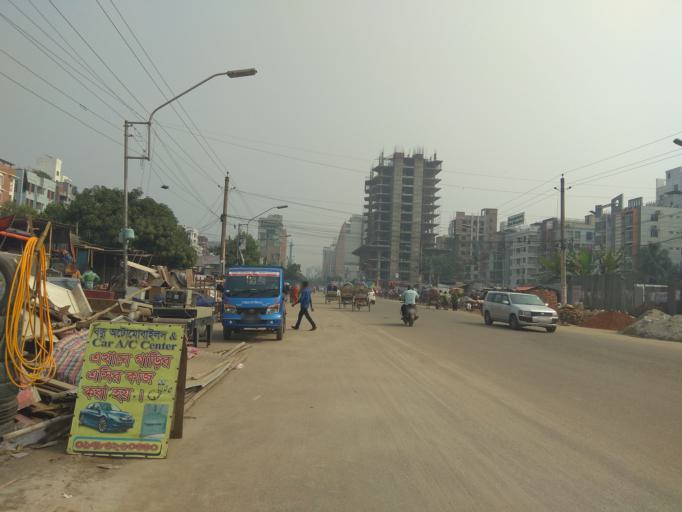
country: BD
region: Dhaka
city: Tungi
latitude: 23.8743
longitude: 90.3868
